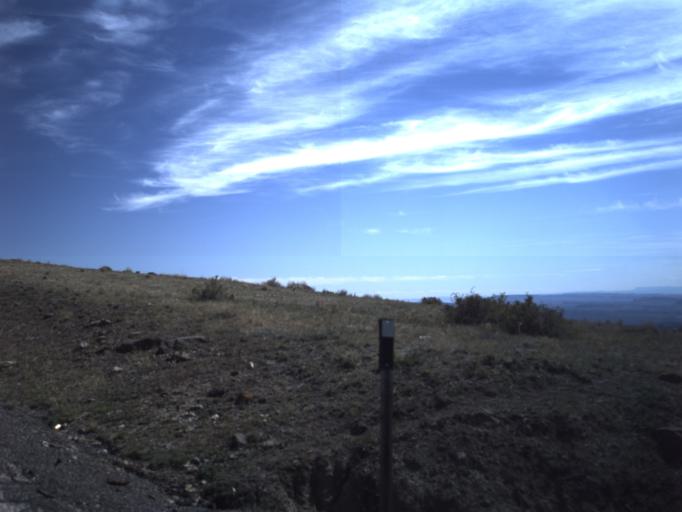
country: US
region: Utah
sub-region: Wayne County
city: Loa
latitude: 38.0263
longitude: -111.3477
